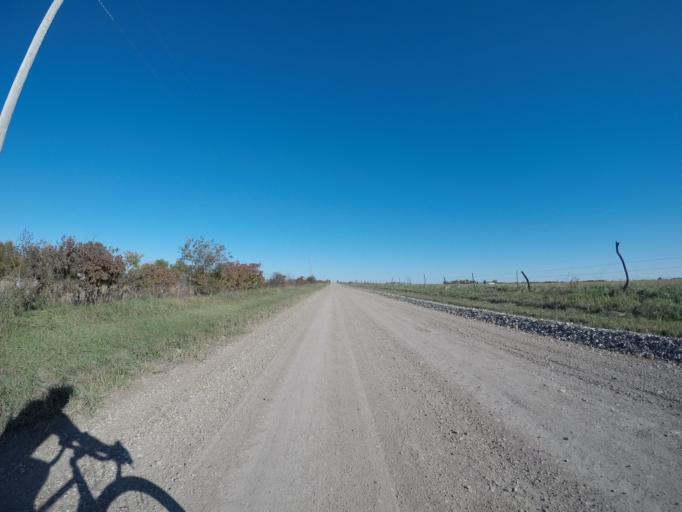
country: US
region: Kansas
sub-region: Morris County
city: Council Grove
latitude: 38.8340
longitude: -96.4087
